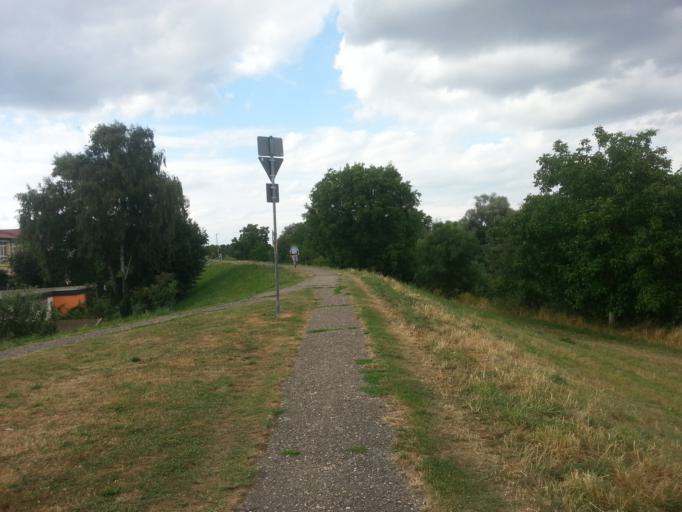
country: DE
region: Baden-Wuerttemberg
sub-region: Karlsruhe Region
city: Ilvesheim
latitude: 49.4703
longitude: 8.5729
